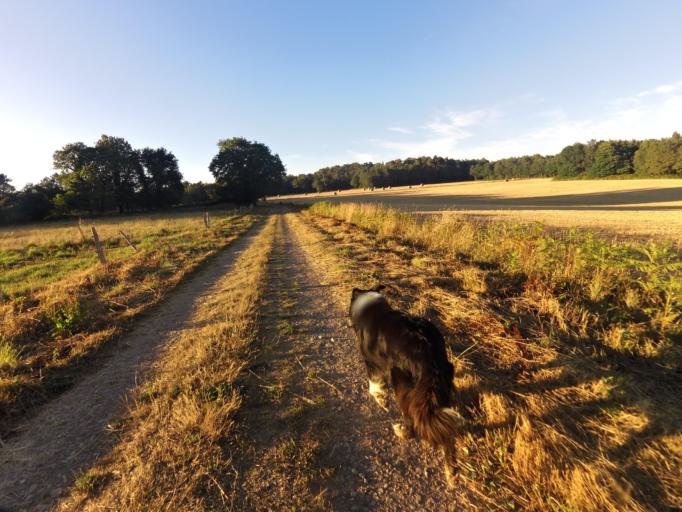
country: FR
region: Brittany
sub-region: Departement du Morbihan
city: Molac
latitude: 47.7032
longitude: -2.4173
